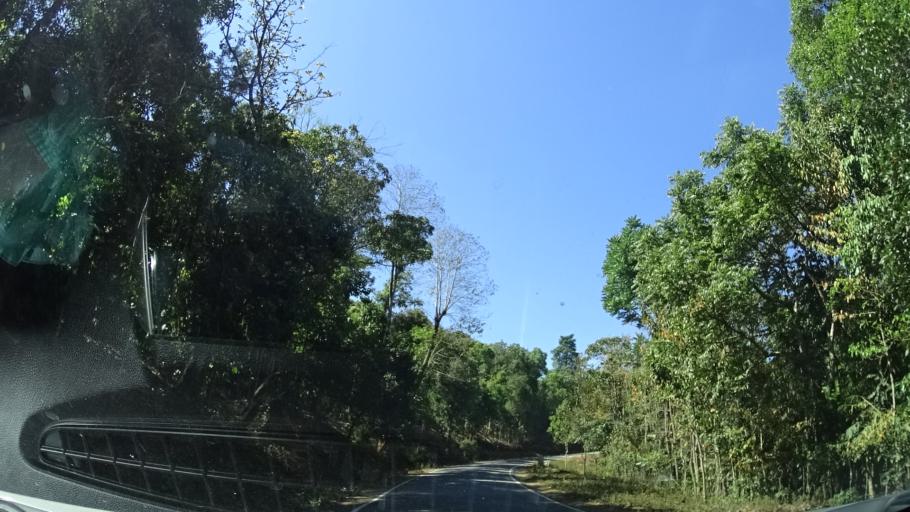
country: IN
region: Karnataka
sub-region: Chikmagalur
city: Sringeri
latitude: 13.2402
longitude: 75.3776
